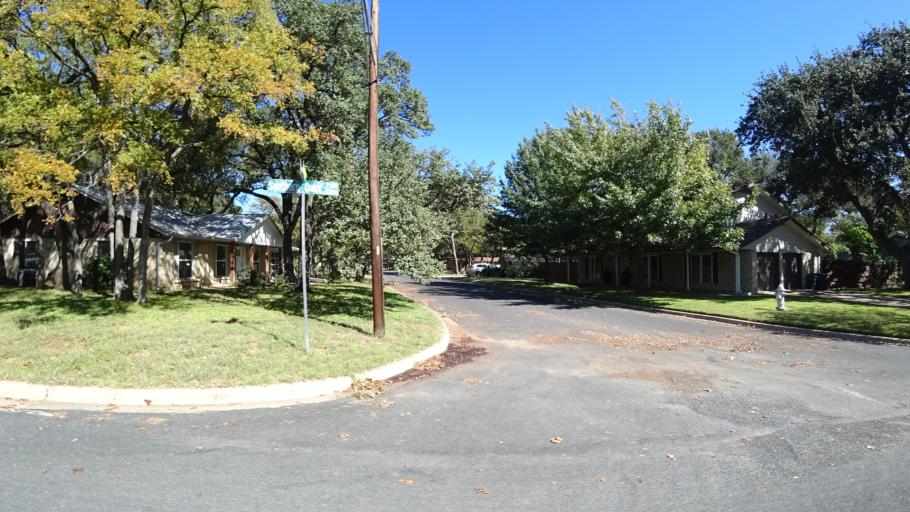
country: US
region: Texas
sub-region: Travis County
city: Rollingwood
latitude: 30.2200
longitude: -97.7978
